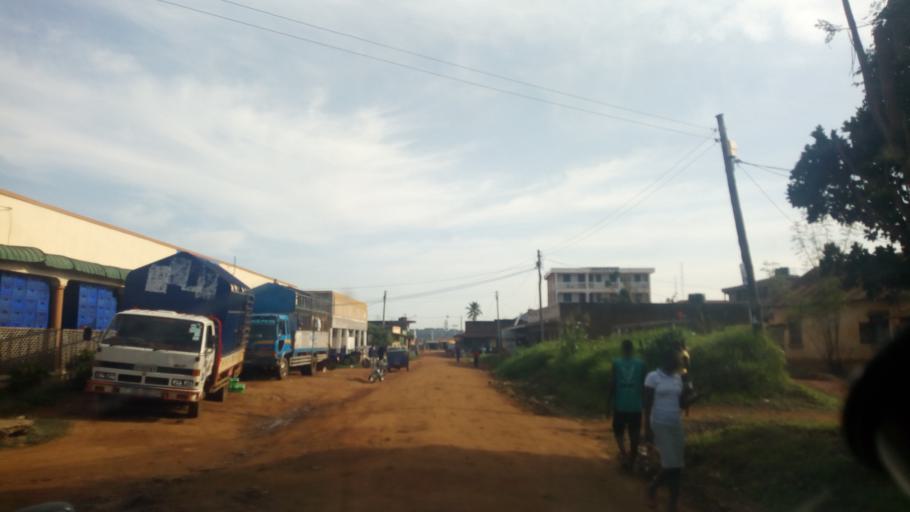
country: UG
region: Northern Region
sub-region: Gulu District
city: Gulu
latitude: 2.7677
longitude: 32.3001
